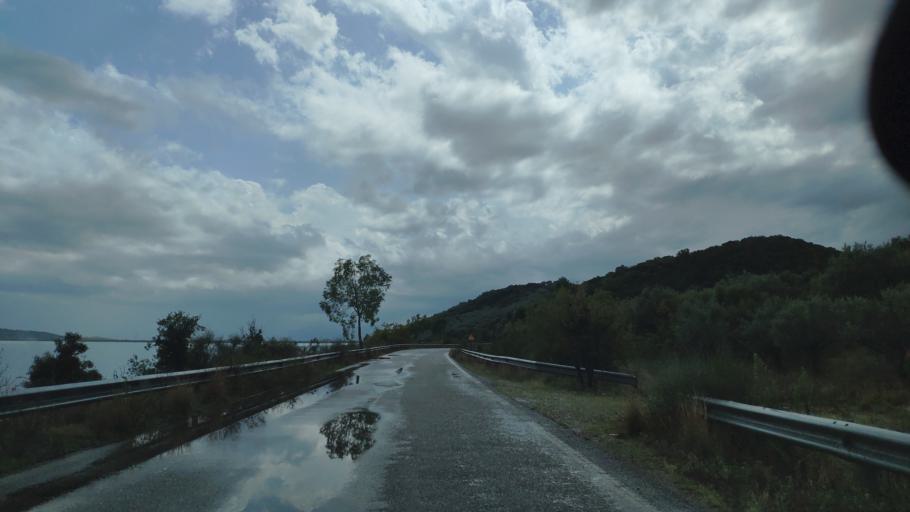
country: GR
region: West Greece
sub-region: Nomos Aitolias kai Akarnanias
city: Lepenou
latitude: 38.6943
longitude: 21.3206
